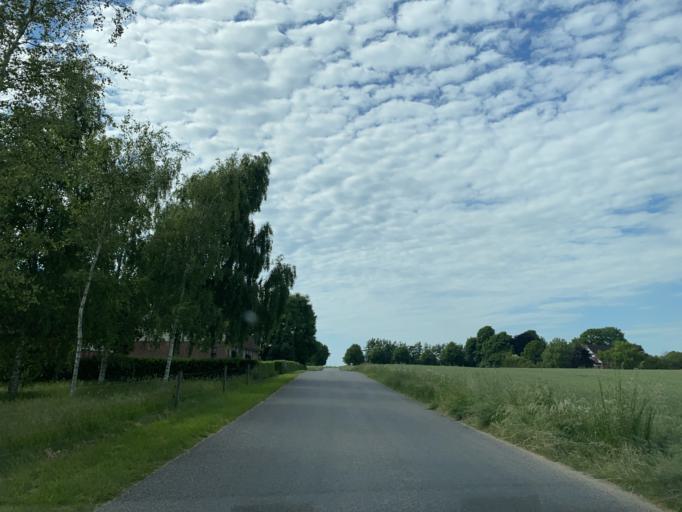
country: DK
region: Central Jutland
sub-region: Favrskov Kommune
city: Hammel
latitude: 56.2088
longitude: 9.8527
